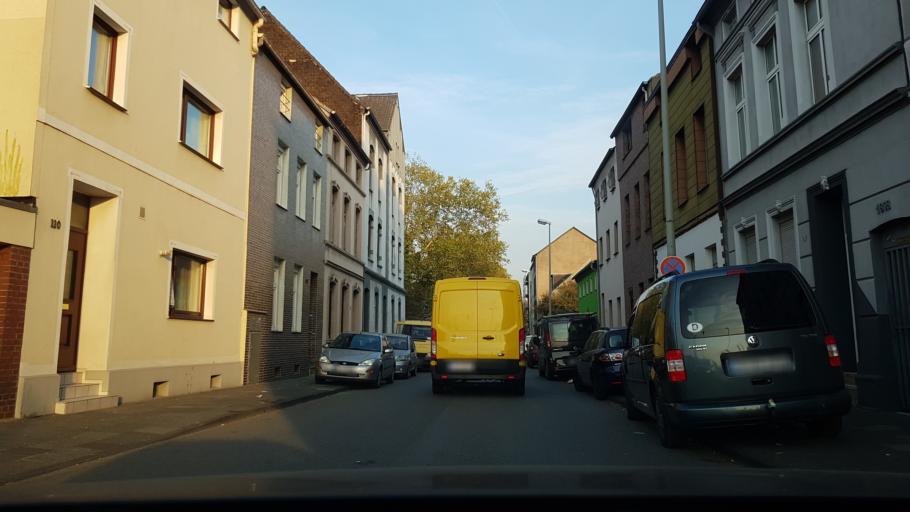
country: DE
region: North Rhine-Westphalia
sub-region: Regierungsbezirk Dusseldorf
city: Hochfeld
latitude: 51.4125
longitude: 6.7531
